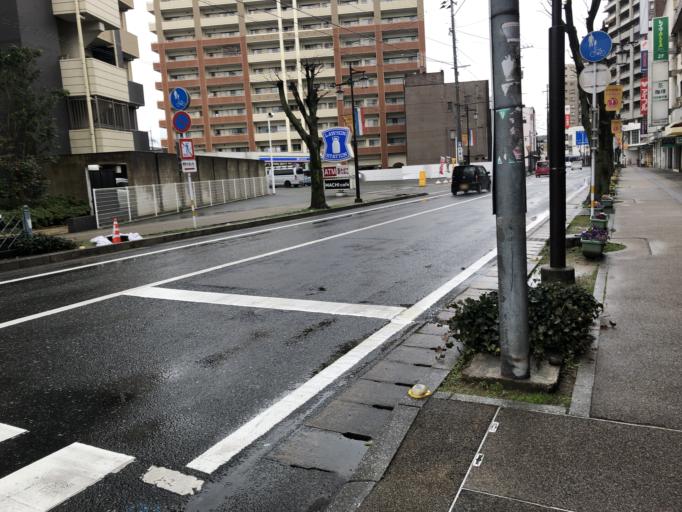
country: JP
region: Oita
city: Hita
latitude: 33.3178
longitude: 130.9372
